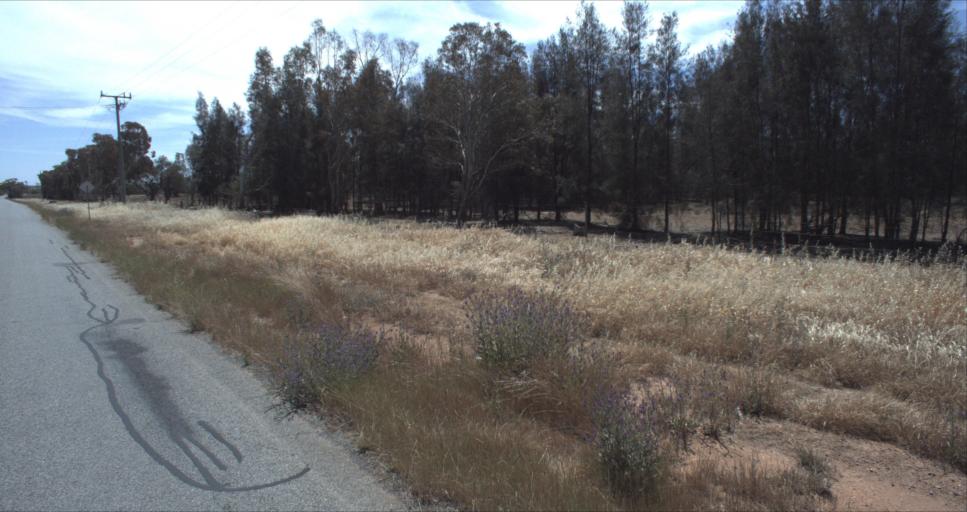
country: AU
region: New South Wales
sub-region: Leeton
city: Leeton
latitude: -34.6455
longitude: 146.4712
